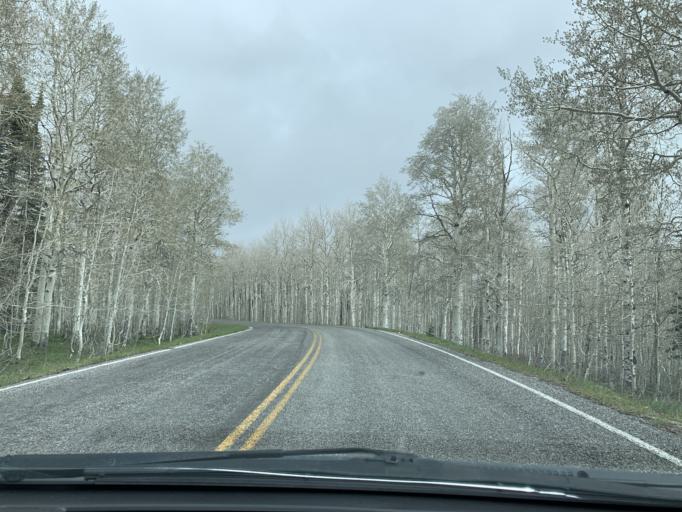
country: US
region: Utah
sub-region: Utah County
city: Elk Ridge
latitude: 39.8763
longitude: -111.6830
